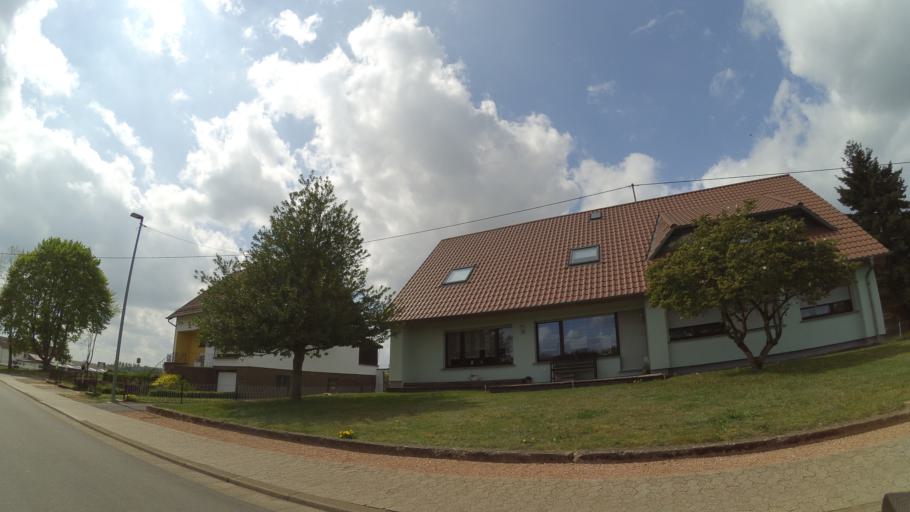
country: DE
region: Saarland
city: Wadern
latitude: 49.5524
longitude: 6.8624
